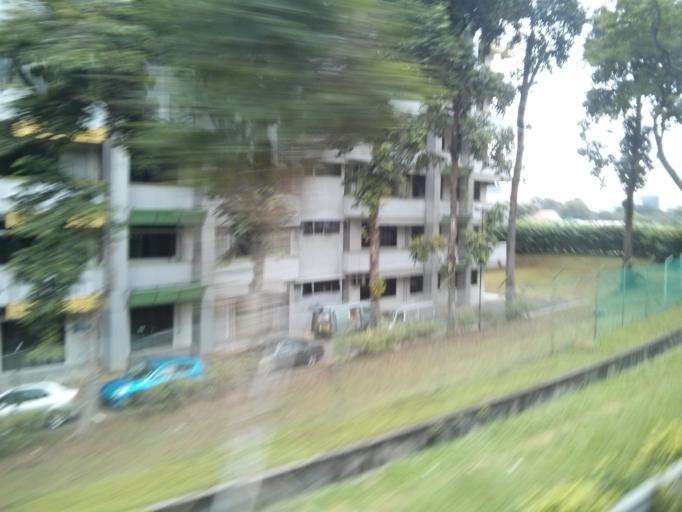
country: SG
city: Singapore
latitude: 1.2930
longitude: 103.7877
